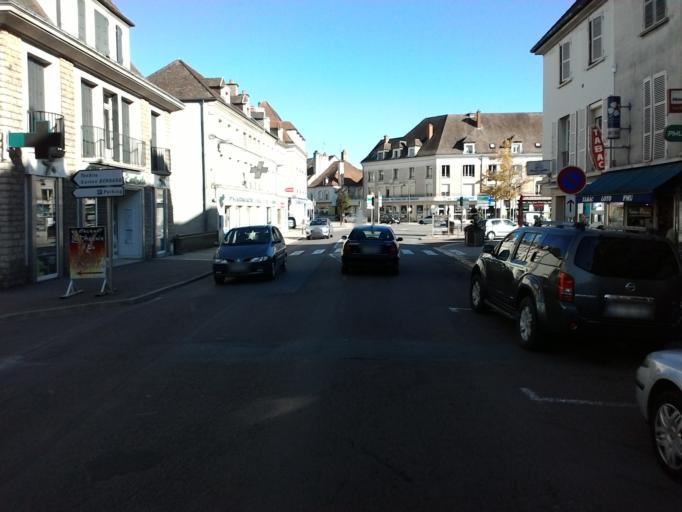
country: FR
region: Bourgogne
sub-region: Departement de la Cote-d'Or
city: Chatillon-sur-Seine
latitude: 47.8597
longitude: 4.5725
